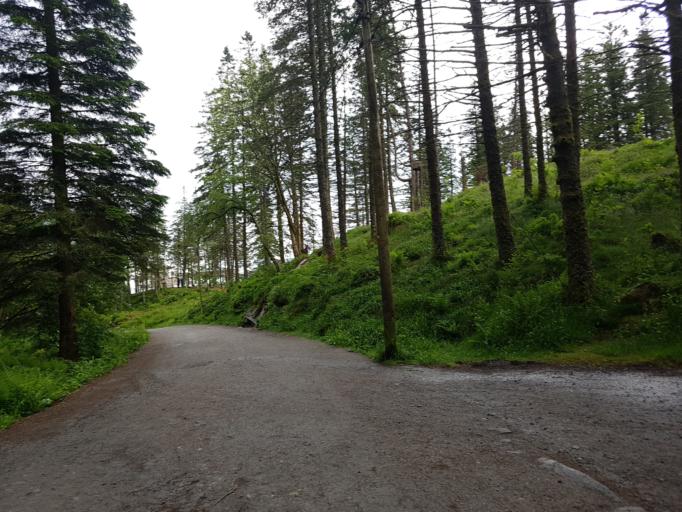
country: NO
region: Hordaland
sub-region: Bergen
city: Bergen
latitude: 60.3960
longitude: 5.3442
